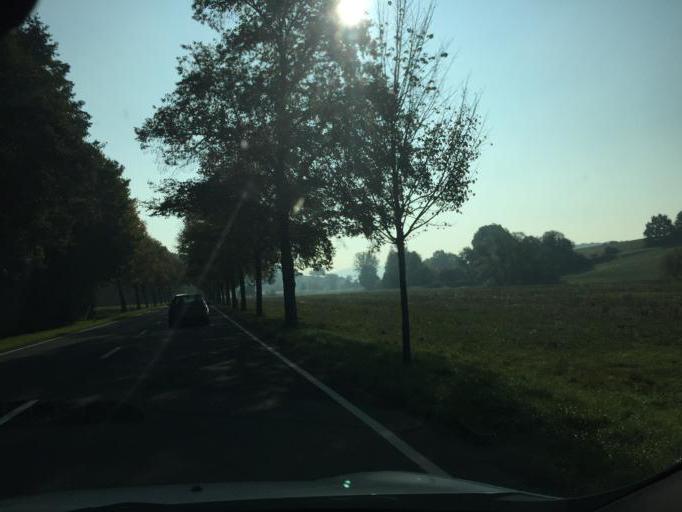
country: LU
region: Grevenmacher
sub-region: Canton de Remich
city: Waldbredimus
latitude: 49.5634
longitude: 6.2982
